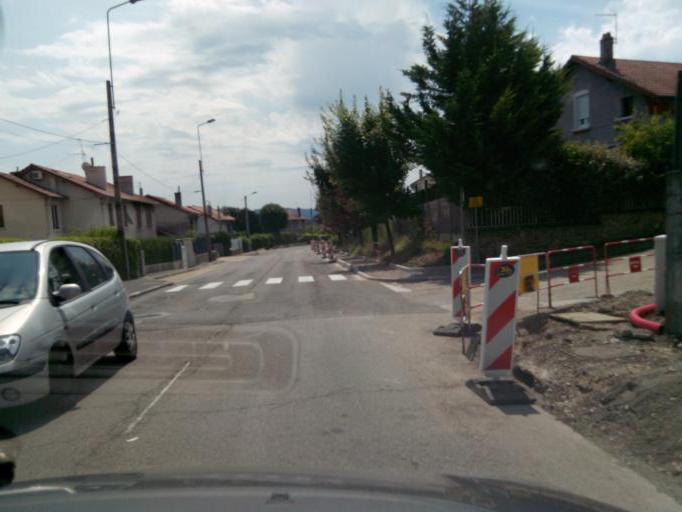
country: FR
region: Rhone-Alpes
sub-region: Departement de la Loire
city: La Ricamarie
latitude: 45.4186
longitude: 4.3124
